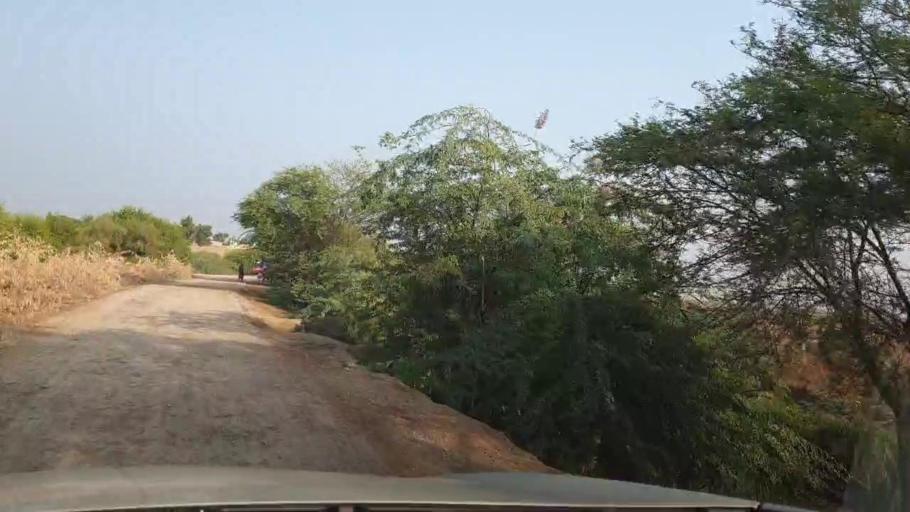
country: PK
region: Sindh
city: Sehwan
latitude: 26.3481
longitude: 67.7233
